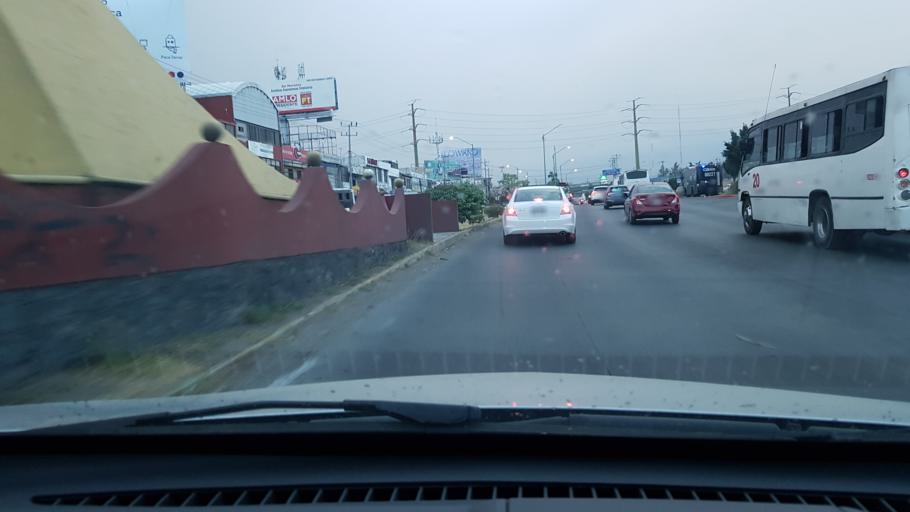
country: MX
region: Morelos
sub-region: Tepoztlan
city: Tetecolala
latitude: 18.9085
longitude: -99.1801
